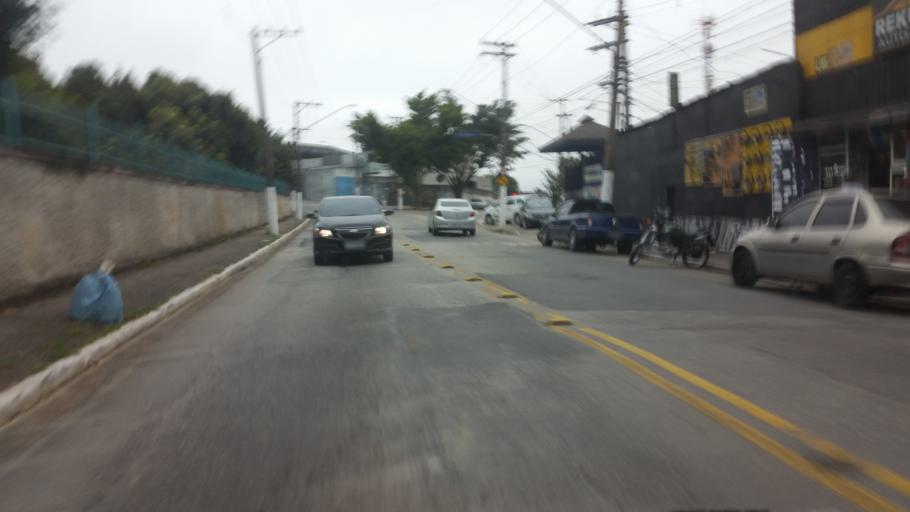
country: BR
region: Sao Paulo
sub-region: Diadema
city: Diadema
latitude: -23.6437
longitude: -46.6126
